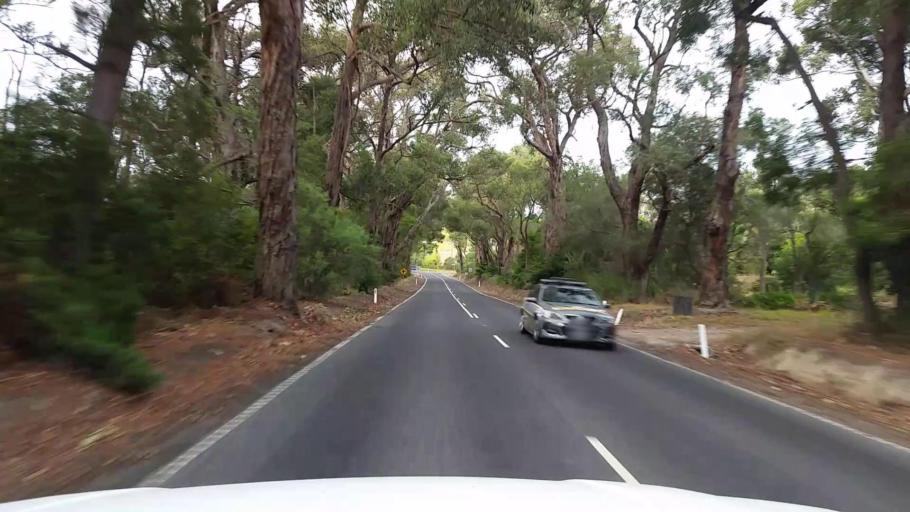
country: AU
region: Victoria
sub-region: Mornington Peninsula
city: Balnarring
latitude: -38.3369
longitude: 145.0964
